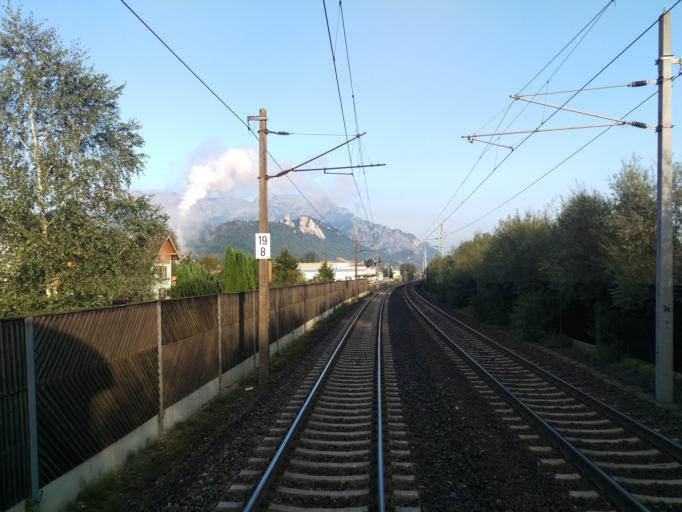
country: AT
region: Salzburg
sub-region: Politischer Bezirk Hallein
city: Adnet
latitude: 47.6728
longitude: 13.1192
